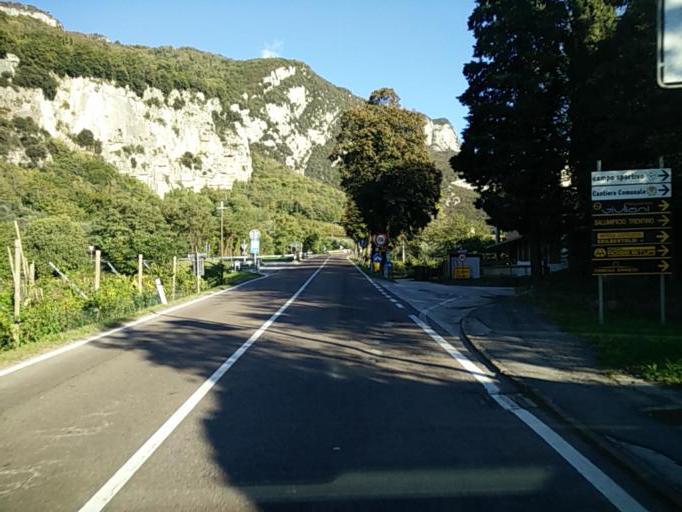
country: IT
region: Trentino-Alto Adige
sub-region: Provincia di Trento
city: Nago-Torbole
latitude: 45.8780
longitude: 10.8991
